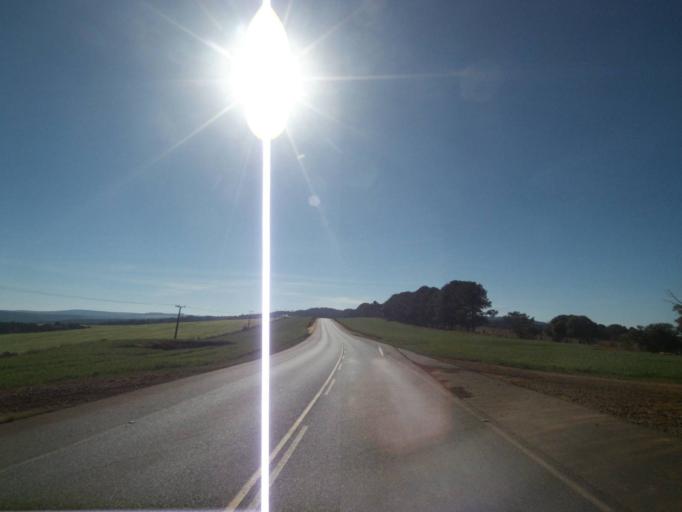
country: BR
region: Parana
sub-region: Tibagi
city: Tibagi
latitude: -24.4223
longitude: -50.3736
